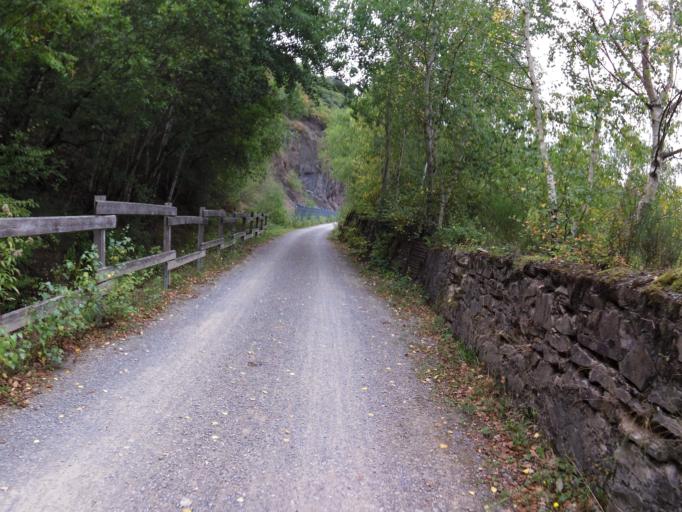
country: DE
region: North Rhine-Westphalia
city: Heimbach
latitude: 50.5971
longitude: 6.4512
